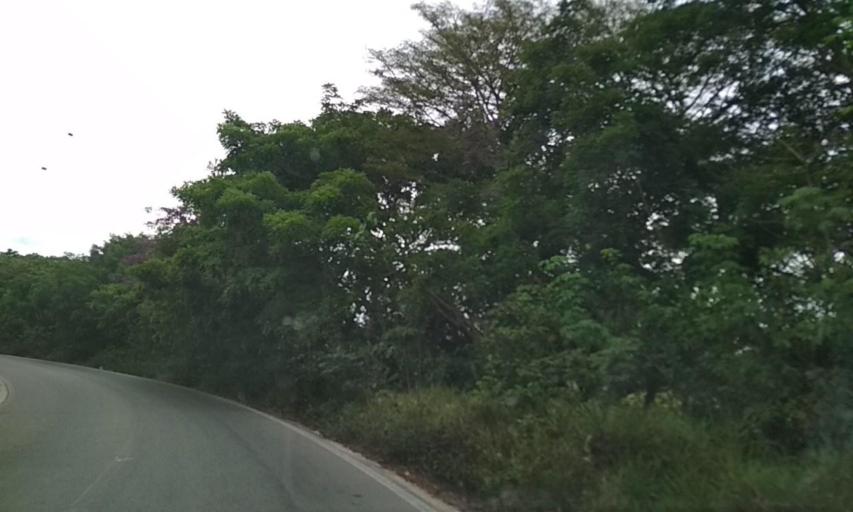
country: MX
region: Veracruz
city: Las Choapas
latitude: 17.8644
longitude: -94.0981
